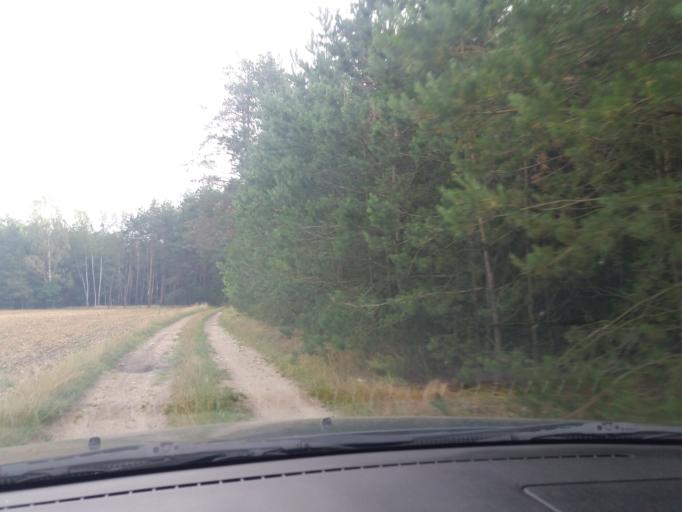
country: PL
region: Masovian Voivodeship
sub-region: Powiat mlawski
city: Wieczfnia Koscielna
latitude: 53.2190
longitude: 20.4581
